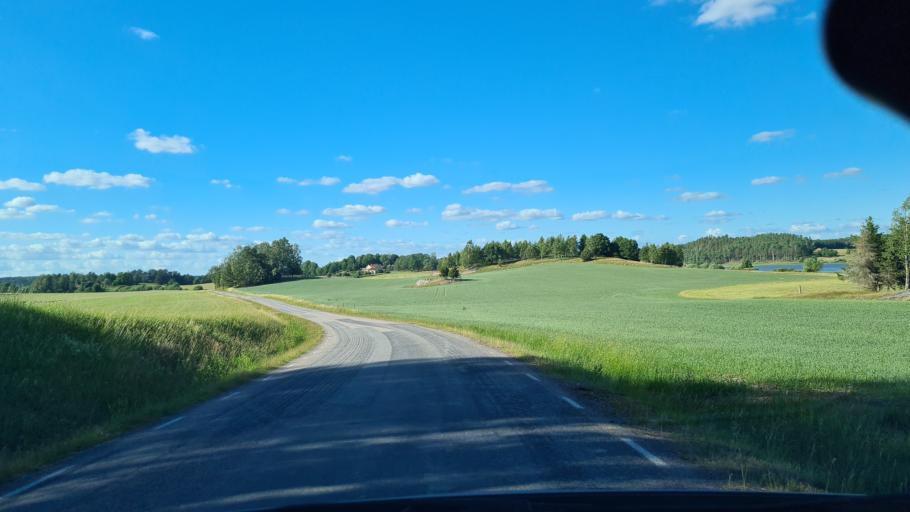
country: SE
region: Soedermanland
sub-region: Nykopings Kommun
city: Stigtomta
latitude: 58.9135
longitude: 16.8802
